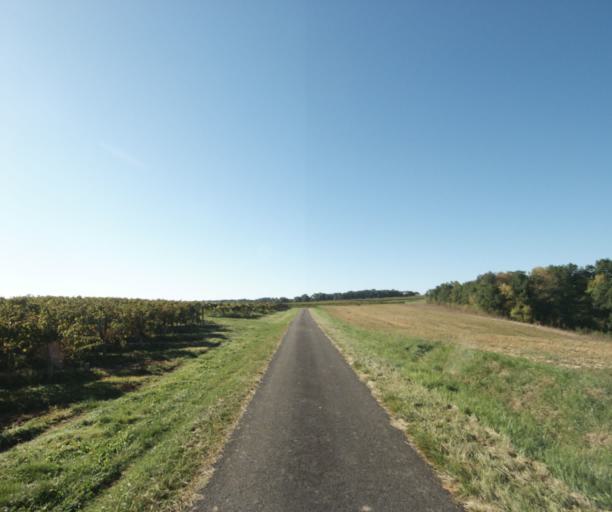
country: FR
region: Midi-Pyrenees
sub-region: Departement du Gers
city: Gondrin
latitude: 43.8252
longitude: 0.2417
